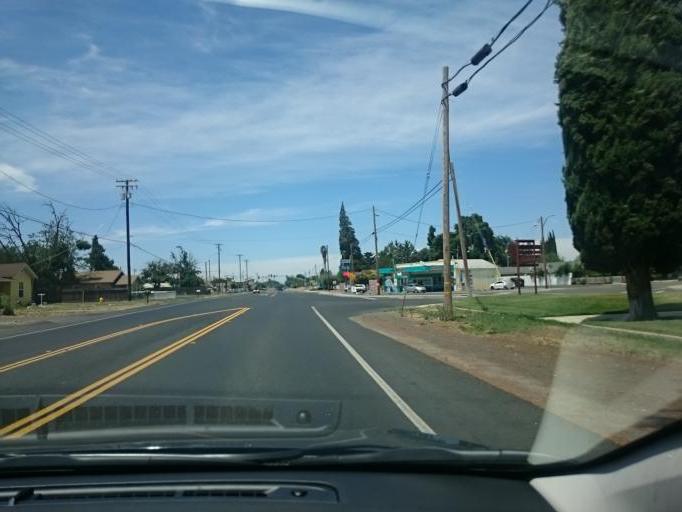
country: US
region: California
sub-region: Stanislaus County
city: Waterford
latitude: 37.6382
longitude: -120.7644
